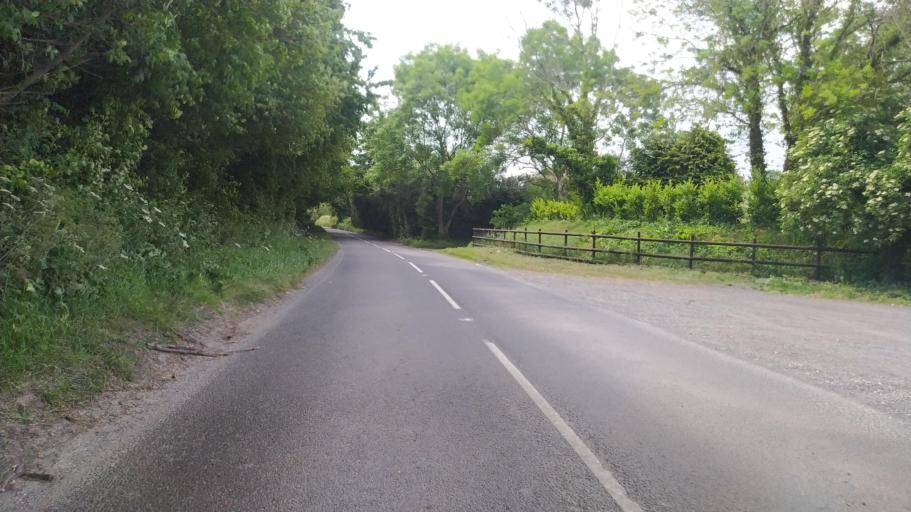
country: GB
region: England
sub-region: Dorset
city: Dorchester
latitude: 50.8036
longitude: -2.4807
